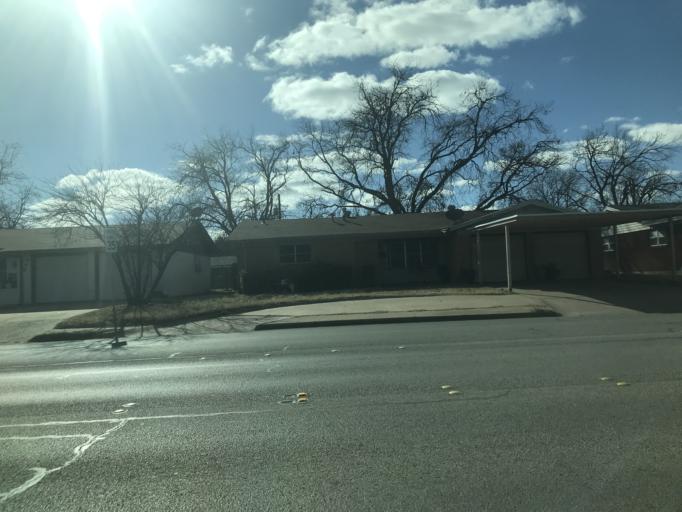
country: US
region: Texas
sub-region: Taylor County
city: Abilene
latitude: 32.4610
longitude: -99.7697
